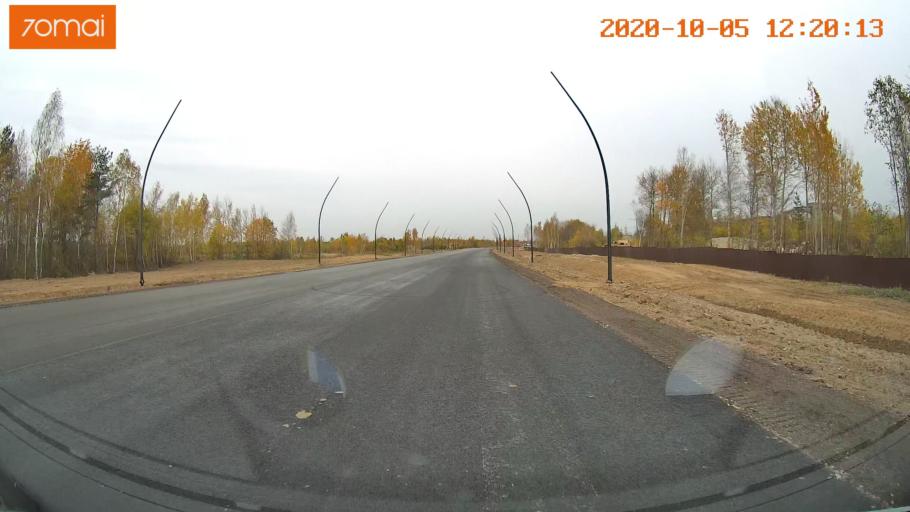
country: RU
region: Ivanovo
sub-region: Gorod Ivanovo
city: Ivanovo
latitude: 56.9610
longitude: 40.9308
